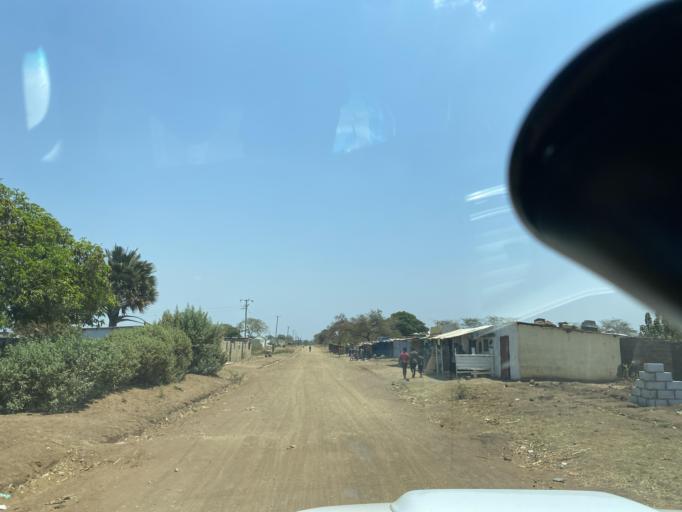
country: ZM
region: Lusaka
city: Lusaka
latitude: -15.4278
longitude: 28.0893
